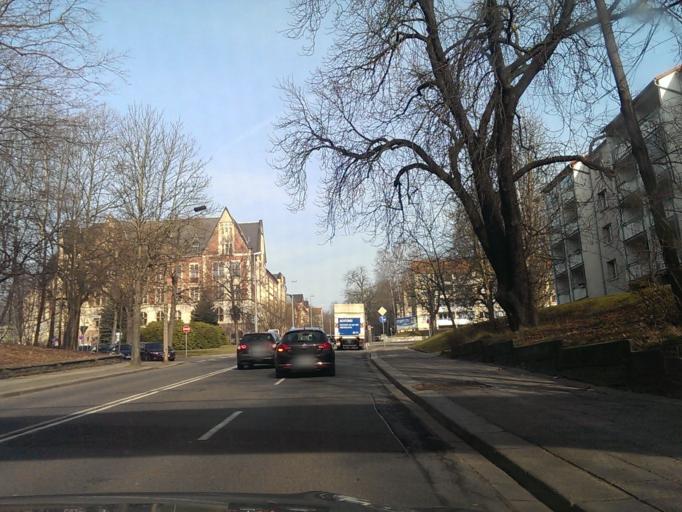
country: DE
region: Saxony
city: Chemnitz
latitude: 50.8290
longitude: 12.9113
